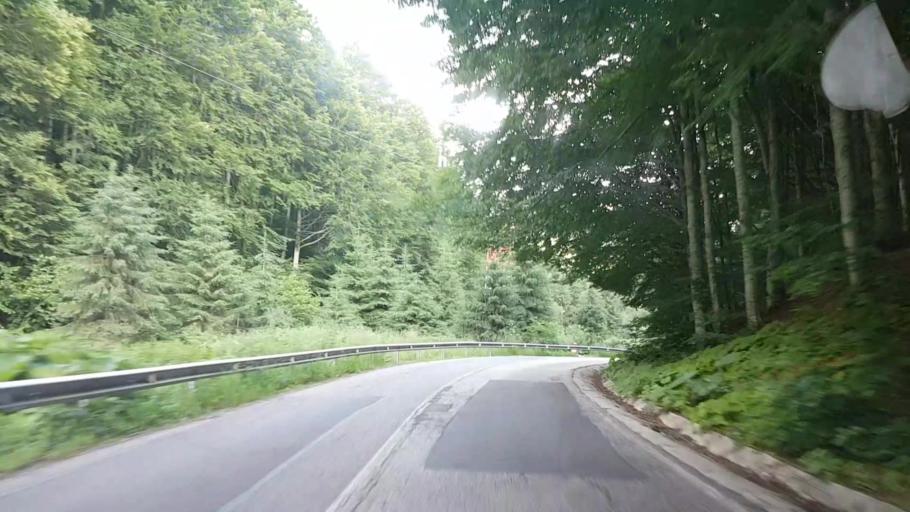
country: RO
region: Harghita
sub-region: Comuna Praid
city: Ocna de Sus
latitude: 46.5956
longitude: 25.2412
